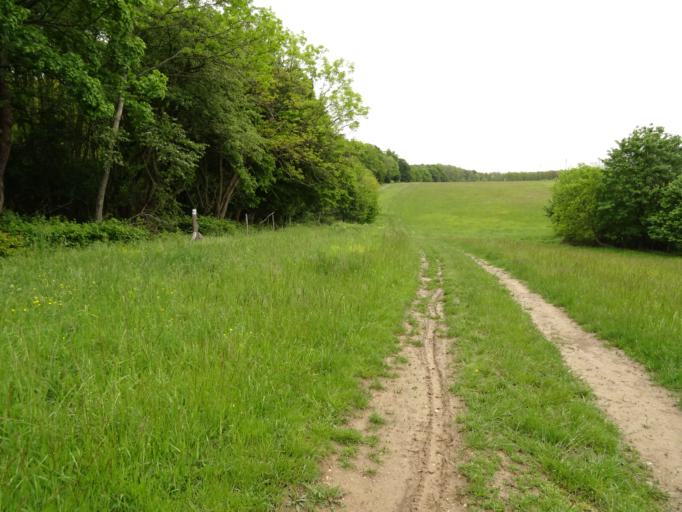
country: HU
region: Veszprem
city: Herend
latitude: 47.1704
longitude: 17.6769
